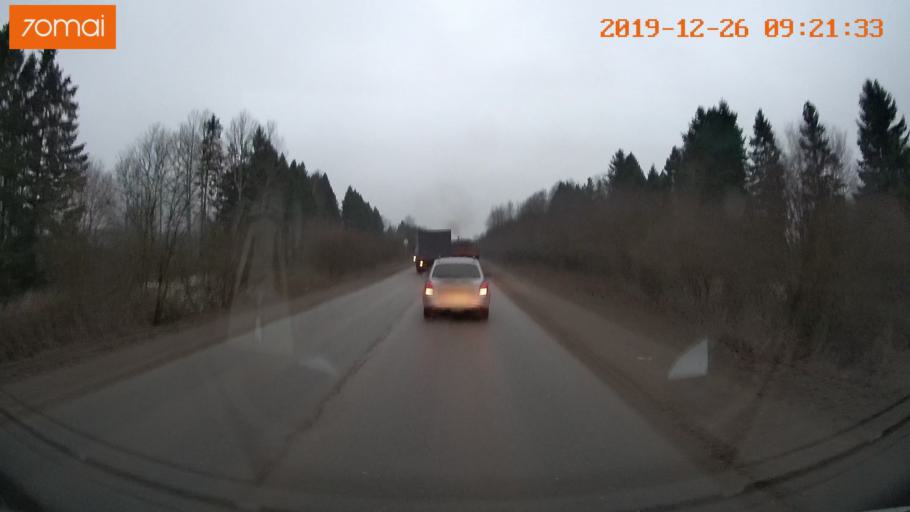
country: RU
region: Vologda
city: Gryazovets
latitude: 58.9708
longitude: 40.2239
